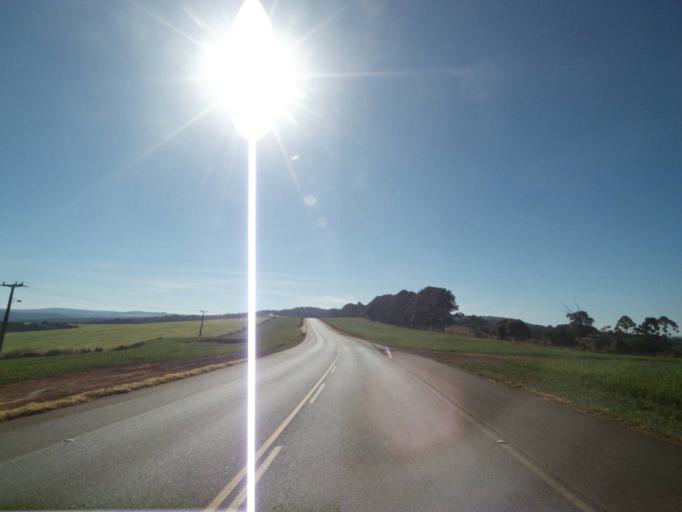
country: BR
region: Parana
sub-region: Tibagi
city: Tibagi
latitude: -24.4225
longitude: -50.3738
